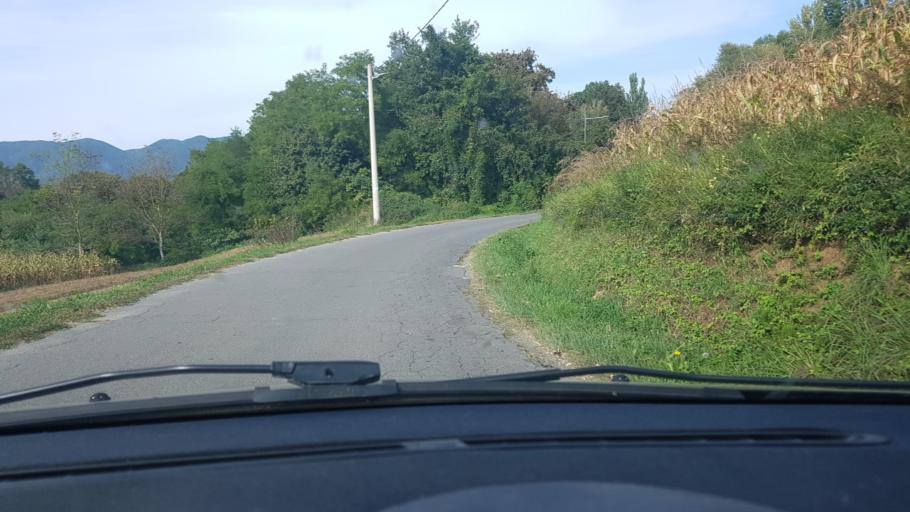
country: HR
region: Krapinsko-Zagorska
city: Zlatar
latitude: 46.1100
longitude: 16.1193
